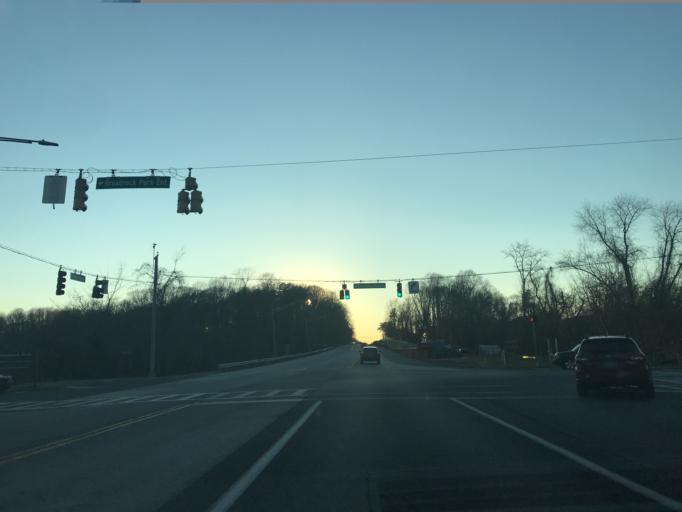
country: US
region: Maryland
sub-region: Anne Arundel County
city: Cape Saint Claire
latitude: 39.0361
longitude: -76.4561
